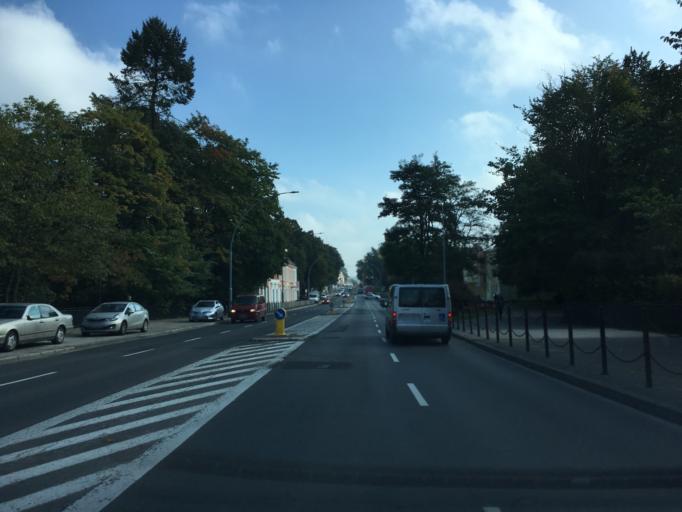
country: PL
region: West Pomeranian Voivodeship
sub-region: Koszalin
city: Koszalin
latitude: 54.1901
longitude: 16.1862
